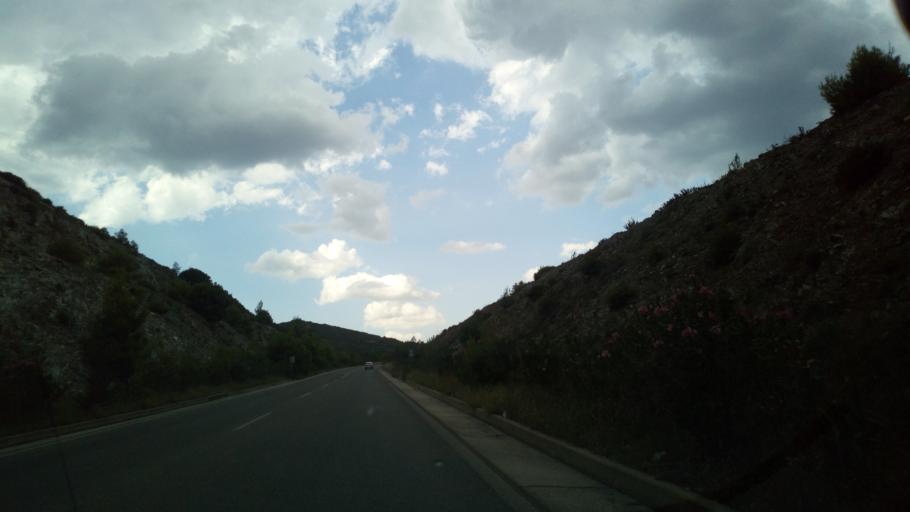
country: GR
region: Central Macedonia
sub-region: Nomos Chalkidikis
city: Polygyros
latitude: 40.3453
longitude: 23.4506
